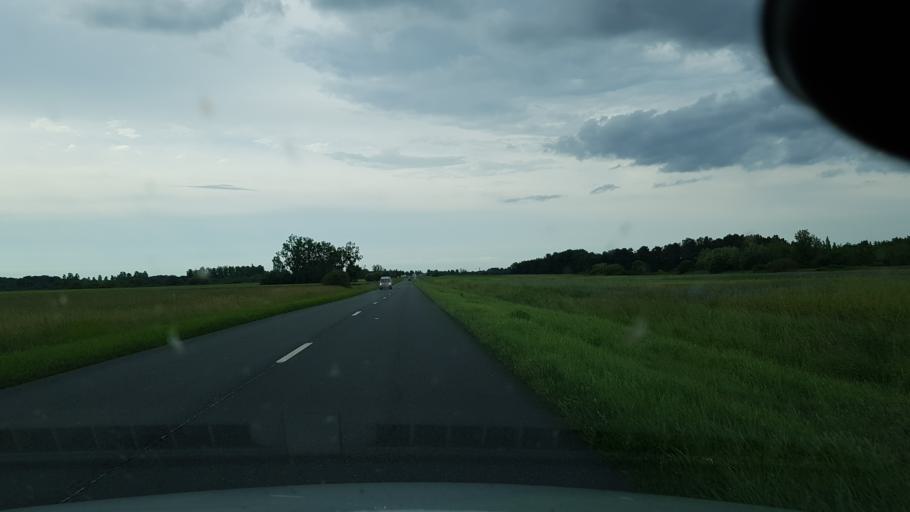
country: FR
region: Centre
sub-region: Departement du Loir-et-Cher
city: Chatillon-sur-Cher
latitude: 47.3136
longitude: 1.5018
